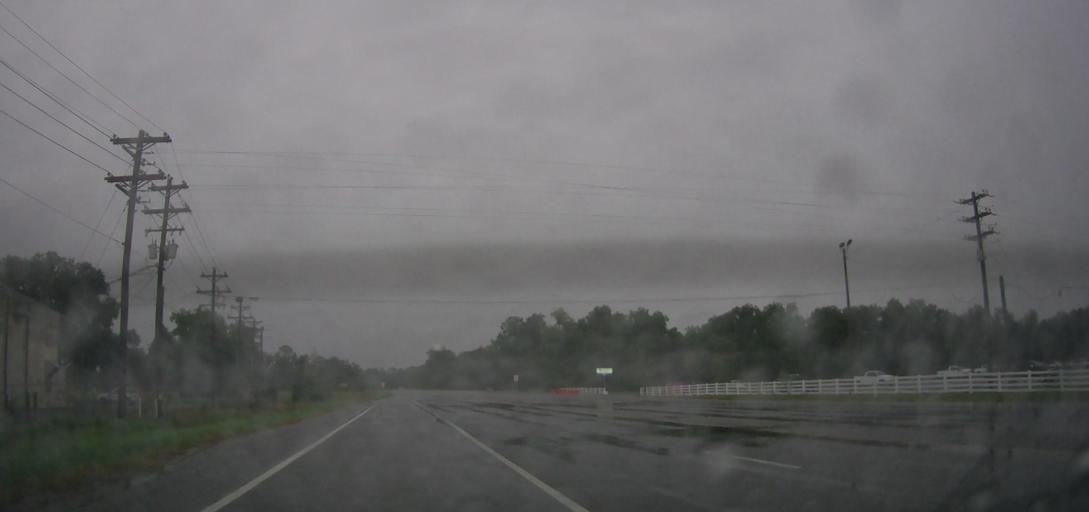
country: US
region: Georgia
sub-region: Clinch County
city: Homerville
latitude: 31.0311
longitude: -82.7732
